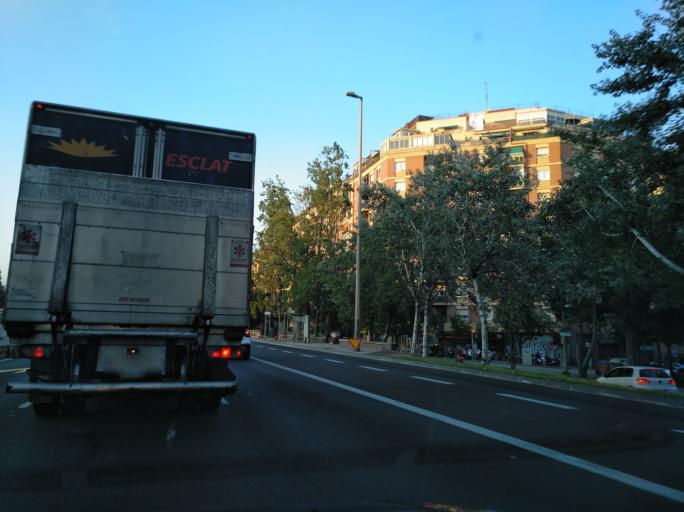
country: ES
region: Catalonia
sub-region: Provincia de Barcelona
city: Sant Andreu de Palomar
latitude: 41.4419
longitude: 2.1861
